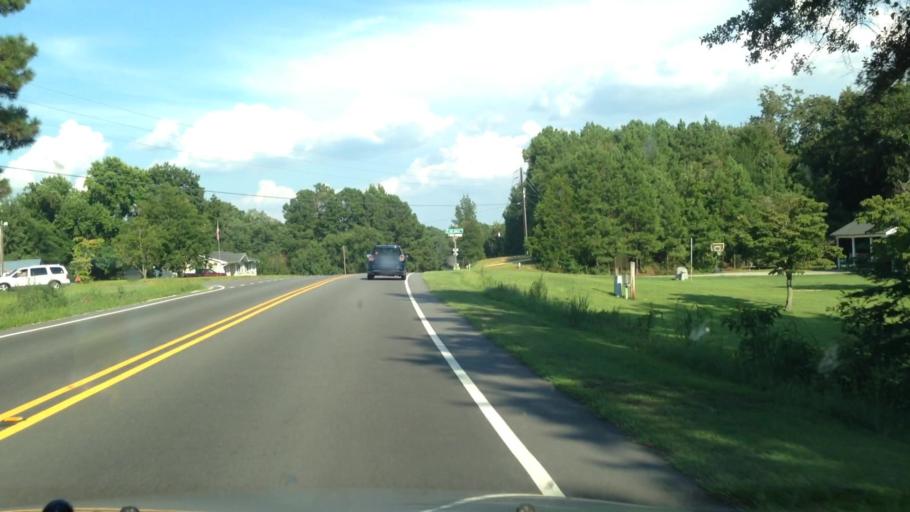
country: US
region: North Carolina
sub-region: Harnett County
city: Coats
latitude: 35.4146
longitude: -78.6983
